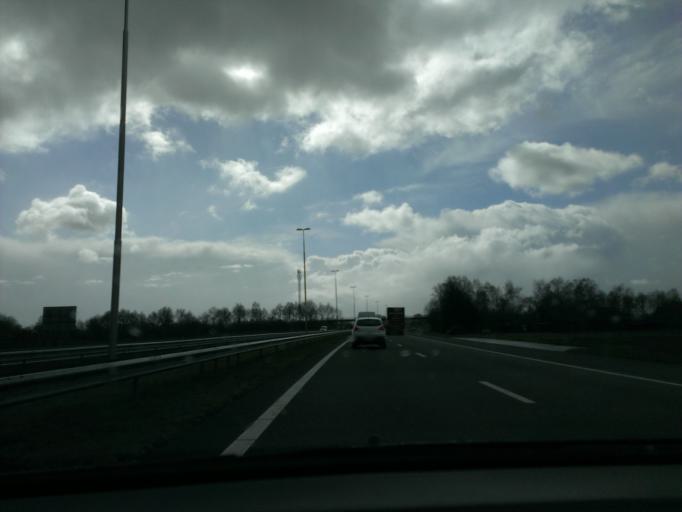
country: NL
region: Gelderland
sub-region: Gemeente Heerde
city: Heerde
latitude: 52.3649
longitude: 6.0259
